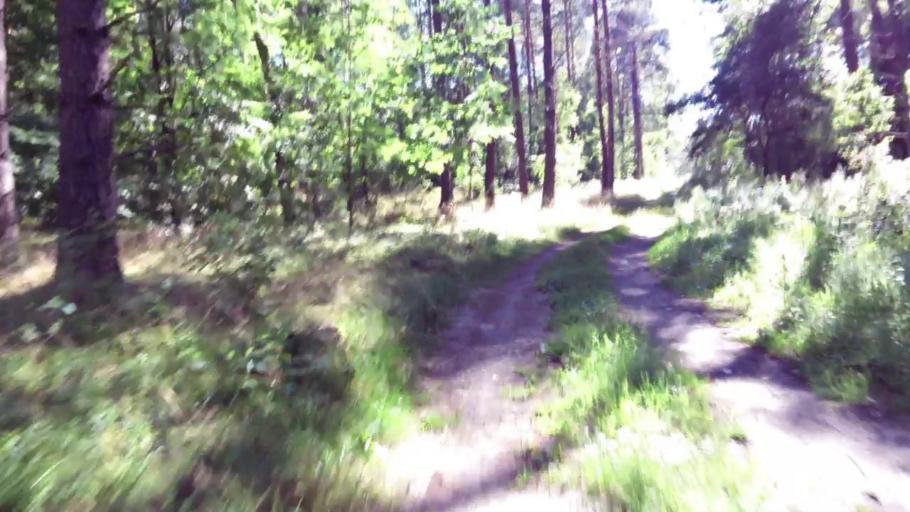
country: PL
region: West Pomeranian Voivodeship
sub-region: Powiat szczecinecki
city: Borne Sulinowo
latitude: 53.6103
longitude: 16.6169
